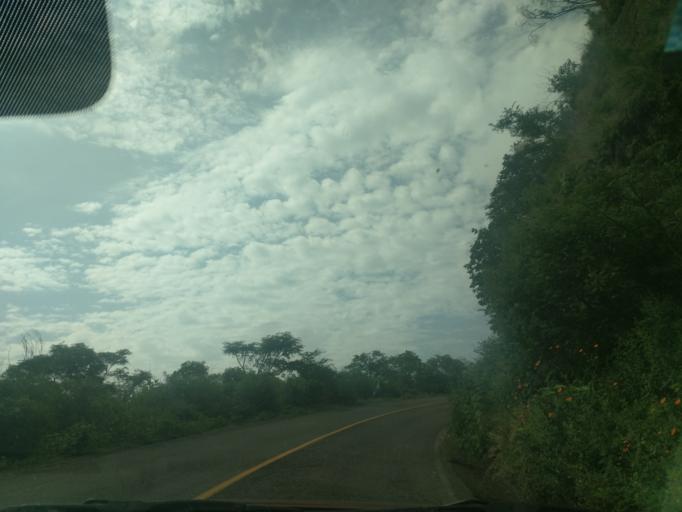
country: MX
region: Jalisco
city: El Salto
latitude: 20.3640
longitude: -104.5836
